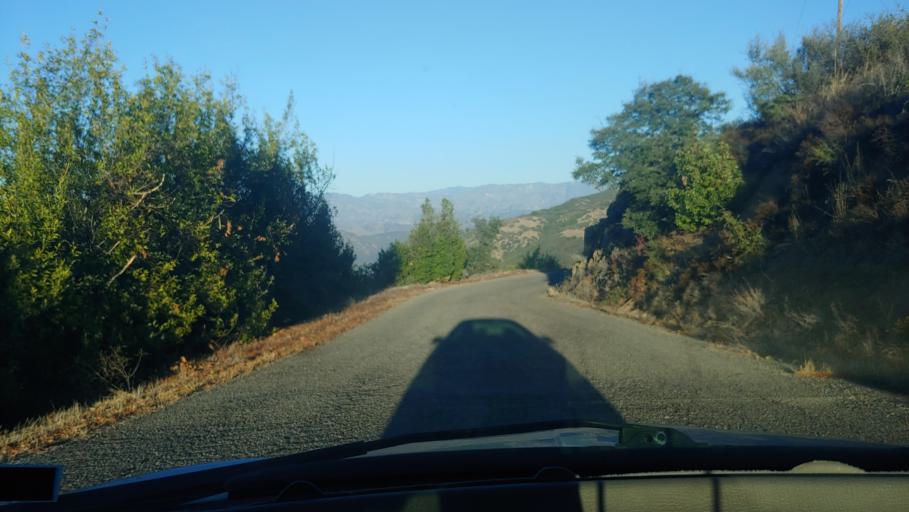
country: US
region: California
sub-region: Santa Barbara County
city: Mission Canyon
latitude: 34.5073
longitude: -119.7634
